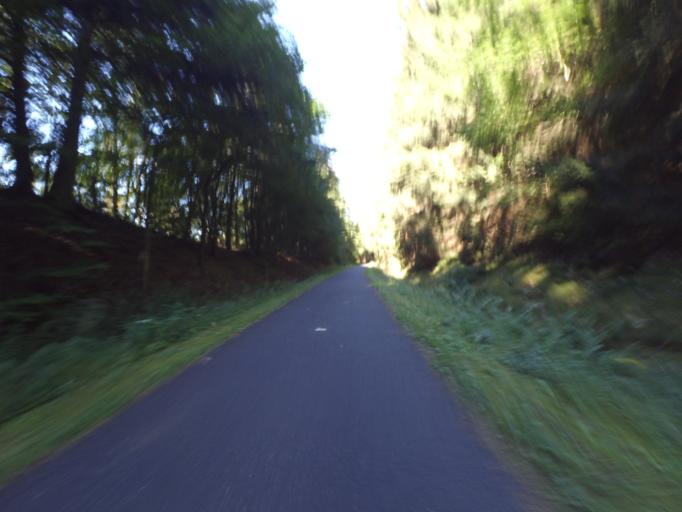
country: DE
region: Rheinland-Pfalz
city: Daun
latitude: 50.1912
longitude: 6.8384
